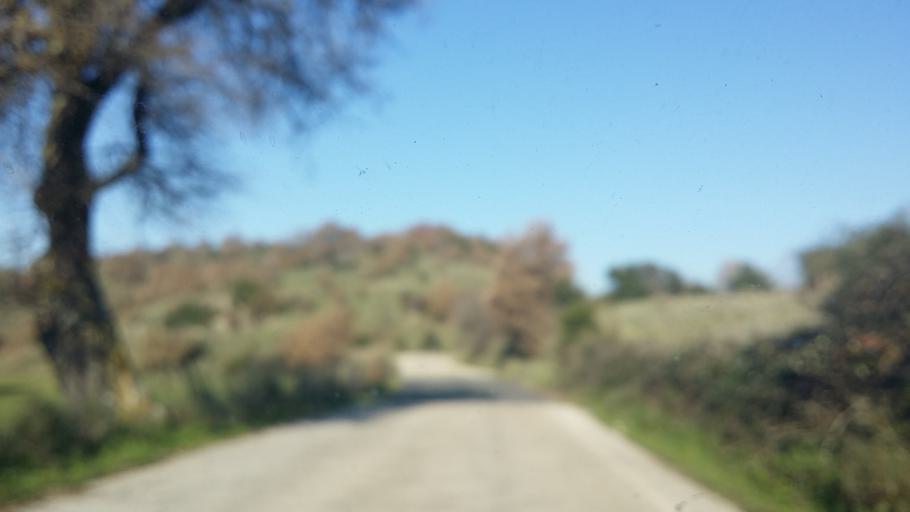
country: GR
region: West Greece
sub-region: Nomos Aitolias kai Akarnanias
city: Katouna
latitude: 38.7963
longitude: 21.1026
